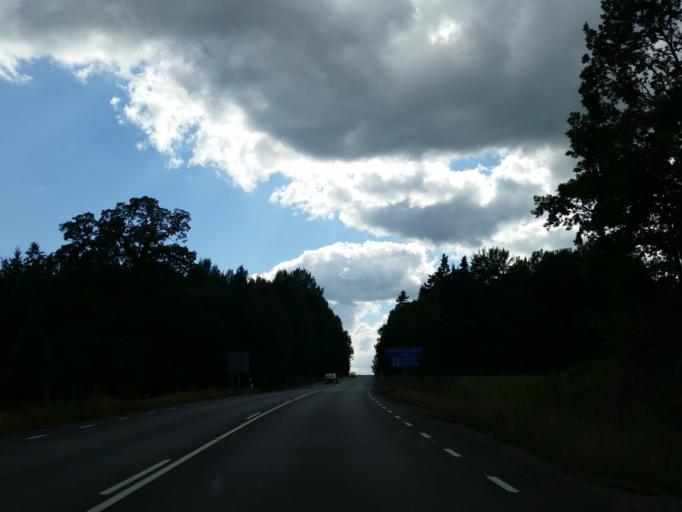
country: SE
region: Soedermanland
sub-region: Trosa Kommun
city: Vagnharad
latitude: 58.9569
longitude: 17.5576
